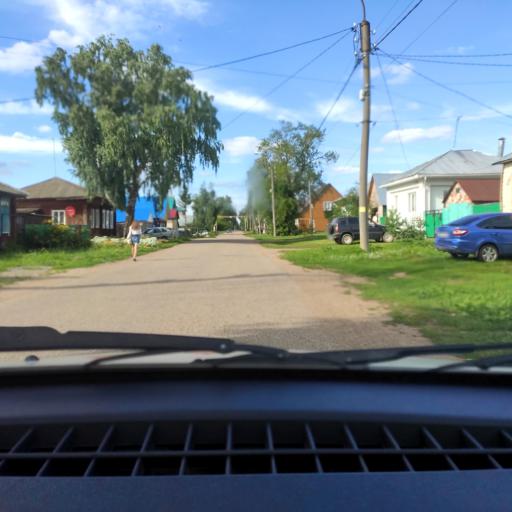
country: RU
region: Bashkortostan
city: Blagoveshchensk
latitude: 55.0280
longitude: 55.9803
